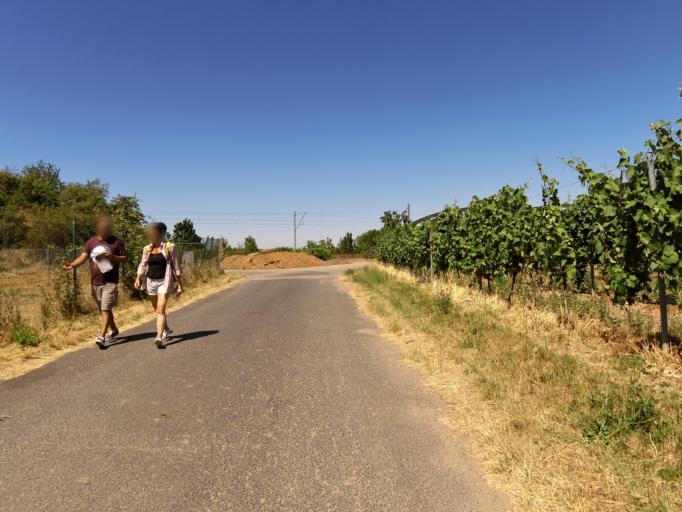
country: DE
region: Rheinland-Pfalz
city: Neustadt
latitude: 49.3585
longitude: 8.1687
